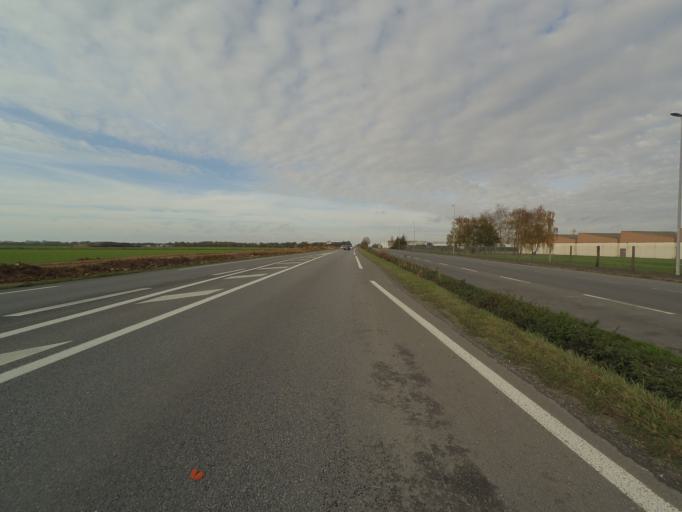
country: FR
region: Pays de la Loire
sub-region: Departement de la Vendee
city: Saint-Hilaire-de-Loulay
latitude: 47.0225
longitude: -1.3466
